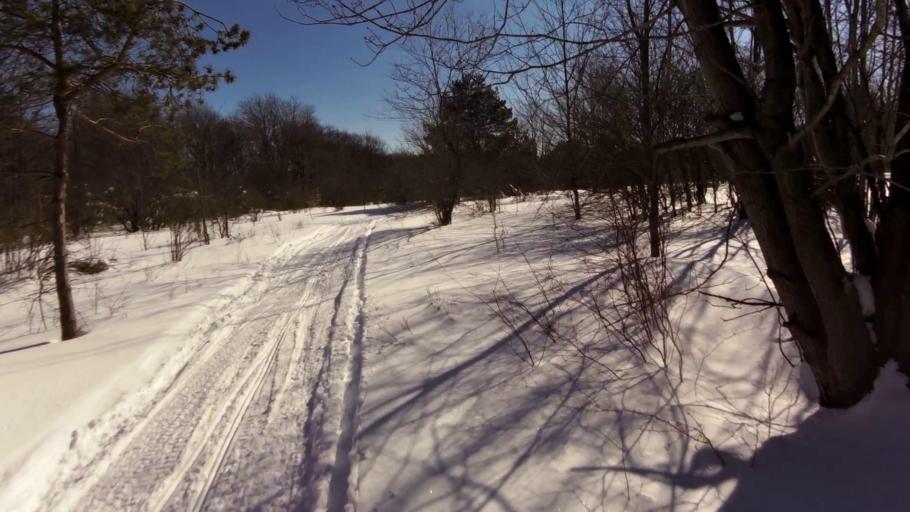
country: US
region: New York
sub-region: Cattaraugus County
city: Franklinville
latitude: 42.3451
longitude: -78.3771
